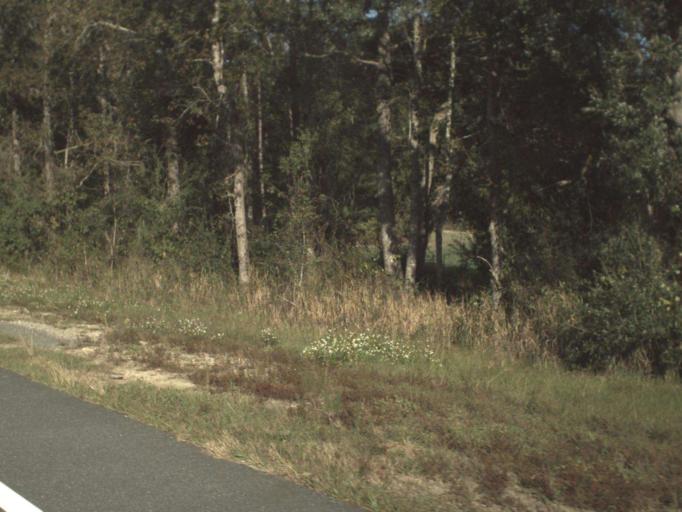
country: US
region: Florida
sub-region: Holmes County
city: Bonifay
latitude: 30.6853
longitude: -85.6326
